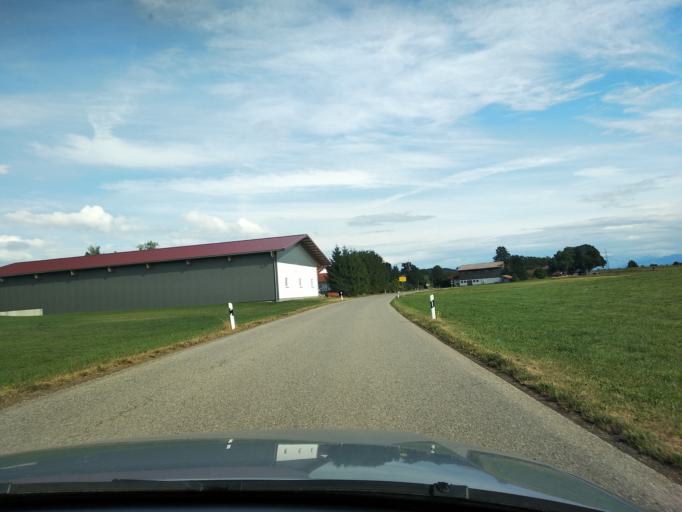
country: DE
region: Bavaria
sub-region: Swabia
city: Dietmannsried
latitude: 47.8202
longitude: 10.3181
